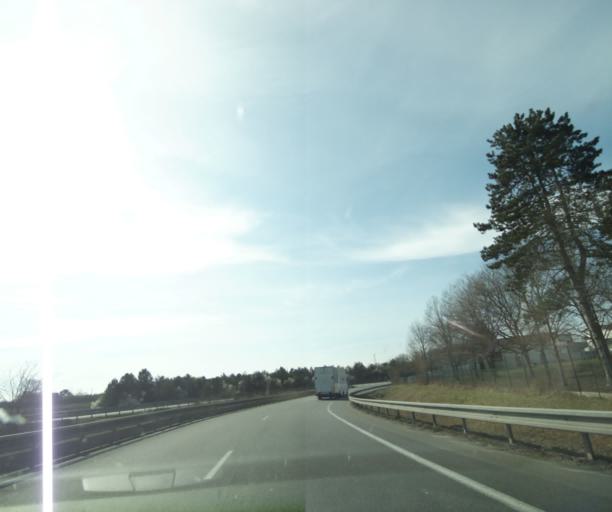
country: FR
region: Centre
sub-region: Departement du Cher
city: Vierzon
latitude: 47.2449
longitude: 2.0706
